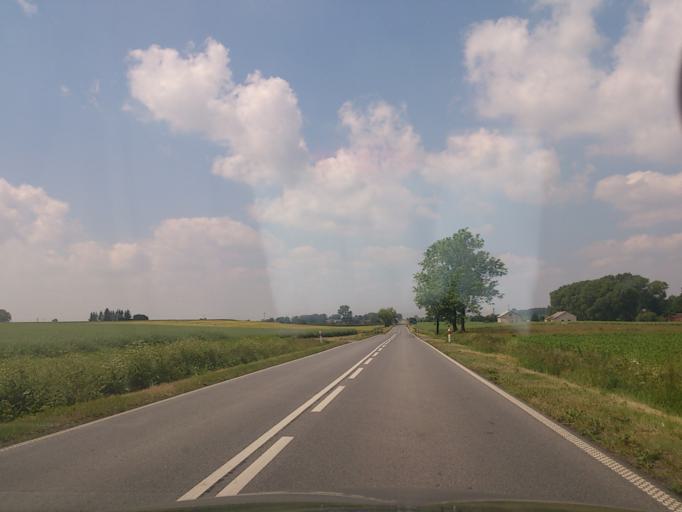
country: PL
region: Kujawsko-Pomorskie
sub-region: Powiat rypinski
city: Brzuze
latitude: 53.0772
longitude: 19.2326
